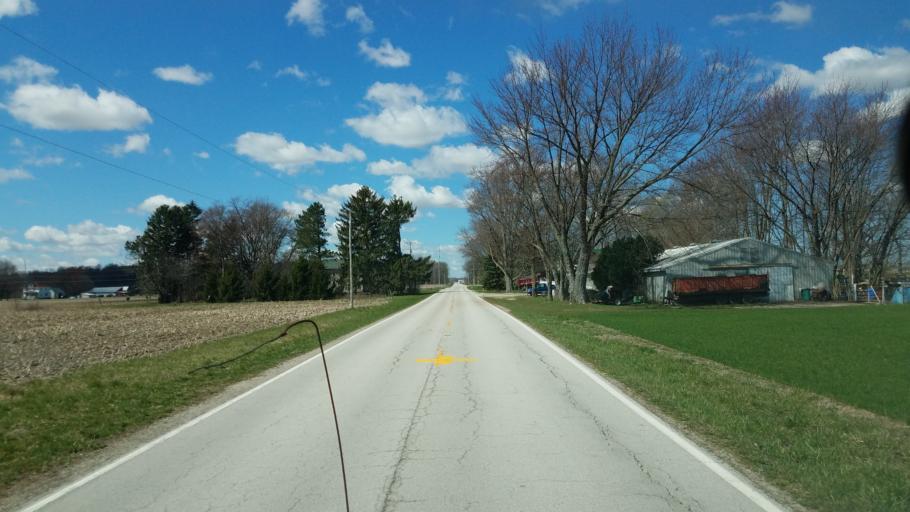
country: US
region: Ohio
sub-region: Sandusky County
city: Green Springs
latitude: 41.2567
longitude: -83.1075
